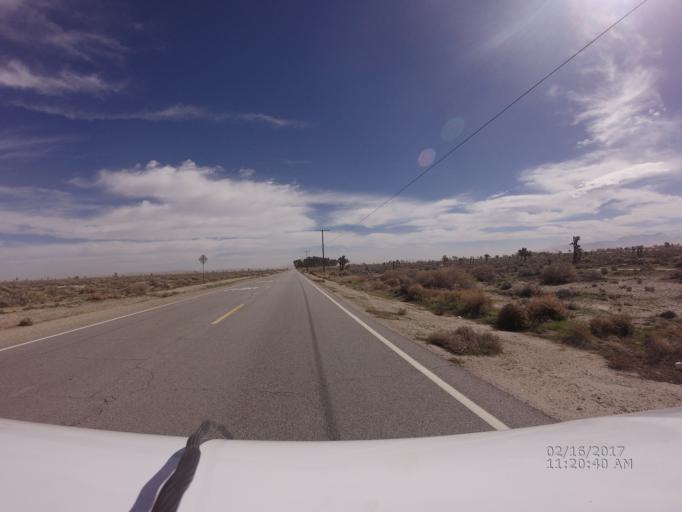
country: US
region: California
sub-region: Los Angeles County
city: Lake Los Angeles
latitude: 34.7049
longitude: -117.9675
